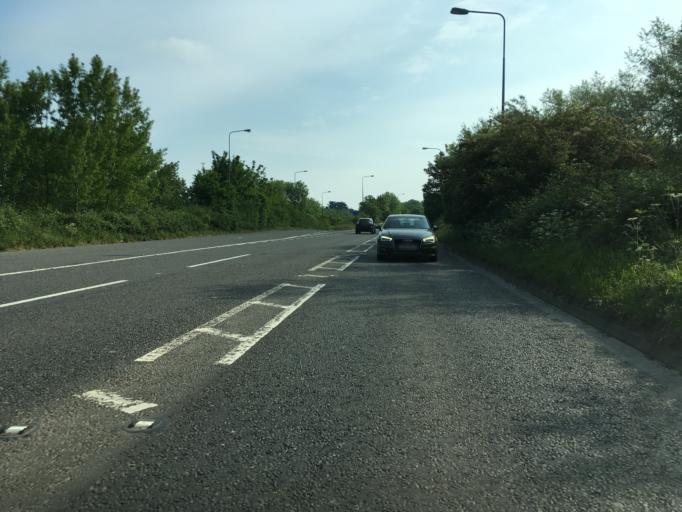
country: GB
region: England
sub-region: North Somerset
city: Long Ashton
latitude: 51.4360
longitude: -2.6387
